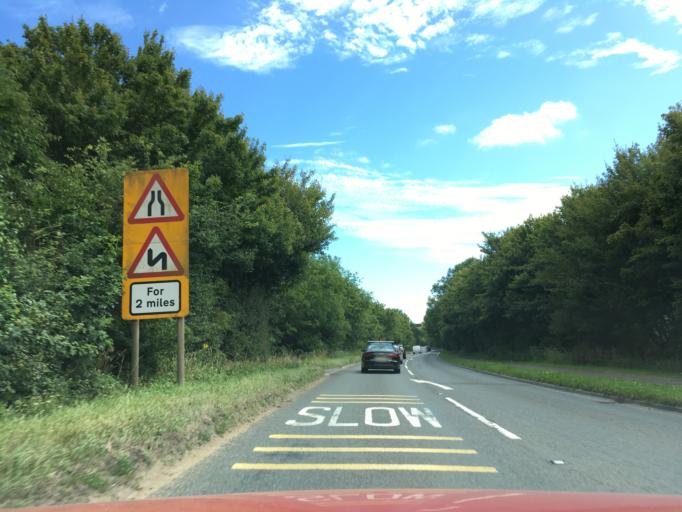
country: GB
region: England
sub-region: Somerset
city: Yeovil
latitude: 50.9180
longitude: -2.6316
